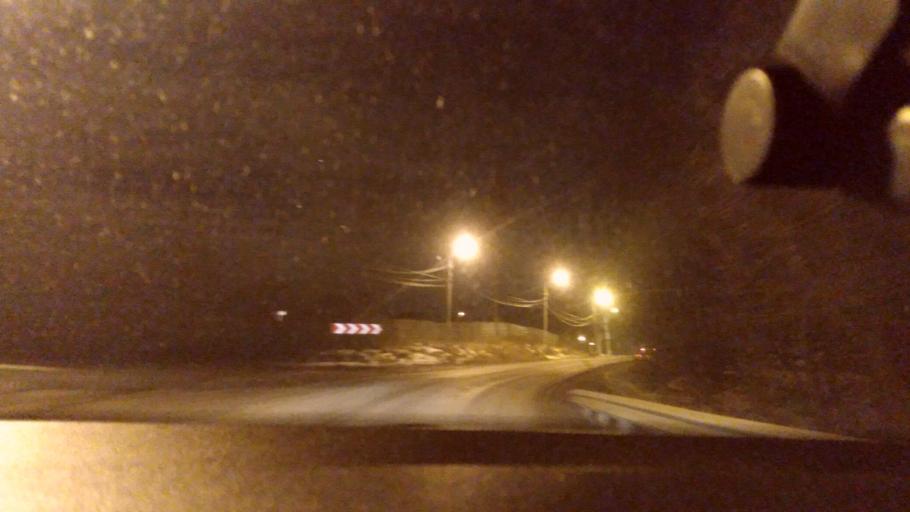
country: RU
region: Moskovskaya
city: Saltykovka
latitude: 55.7790
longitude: 37.9316
